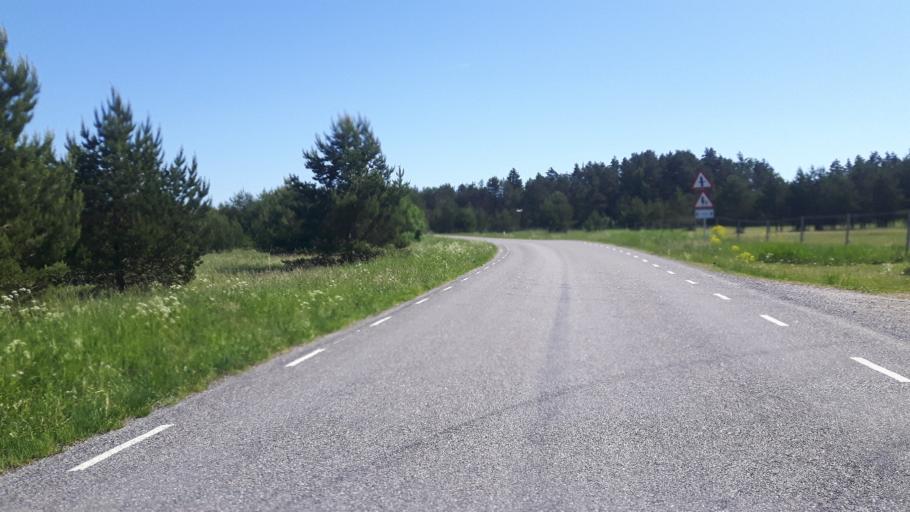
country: EE
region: Raplamaa
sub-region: Kohila vald
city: Kohila
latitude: 59.1942
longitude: 24.7001
